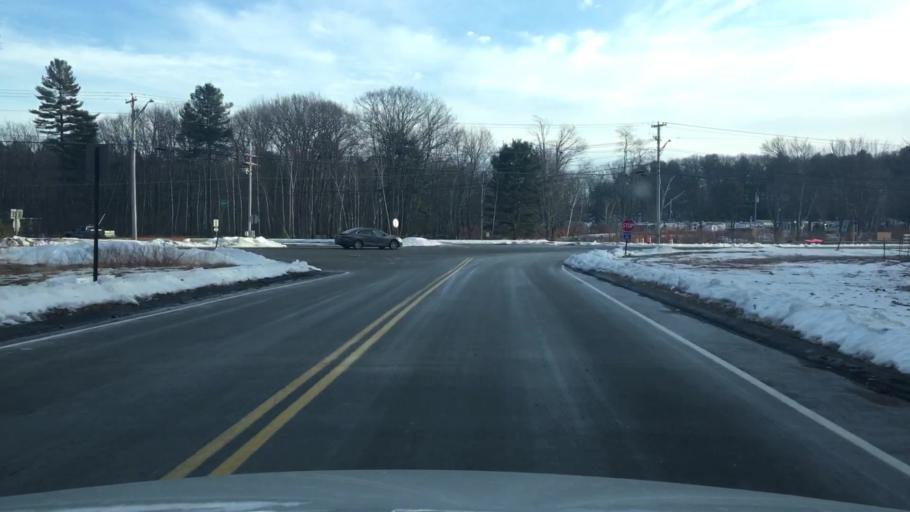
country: US
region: Maine
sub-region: York County
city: Wells Beach Station
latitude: 43.3453
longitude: -70.5614
